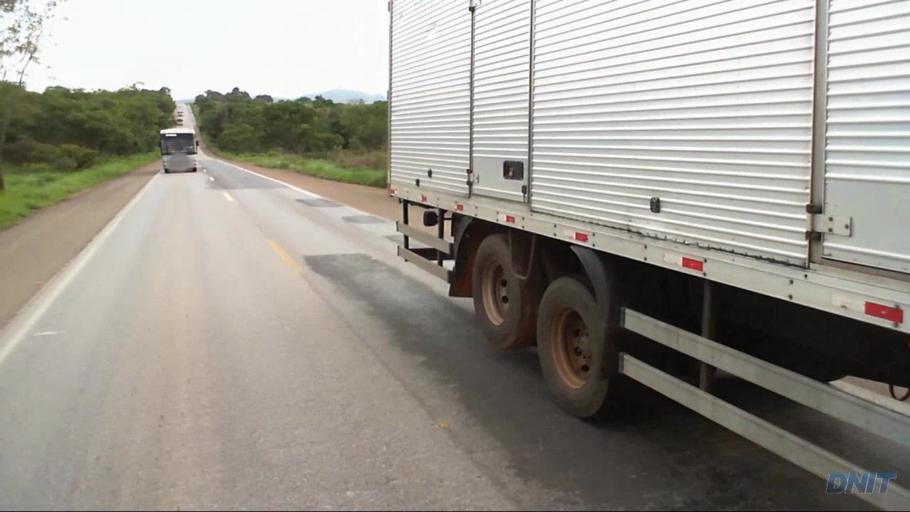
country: BR
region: Goias
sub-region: Uruacu
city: Uruacu
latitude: -14.6159
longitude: -49.1698
